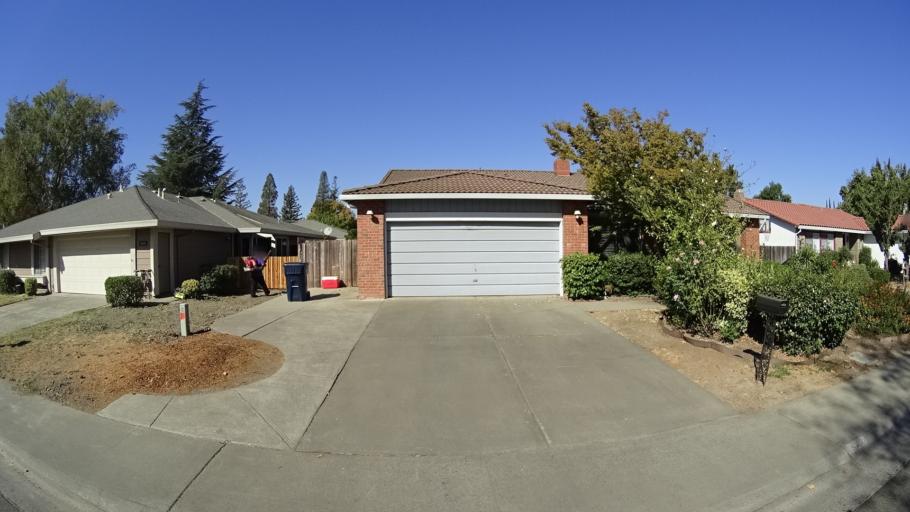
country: US
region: California
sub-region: Yolo County
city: West Sacramento
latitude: 38.5047
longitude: -121.5445
